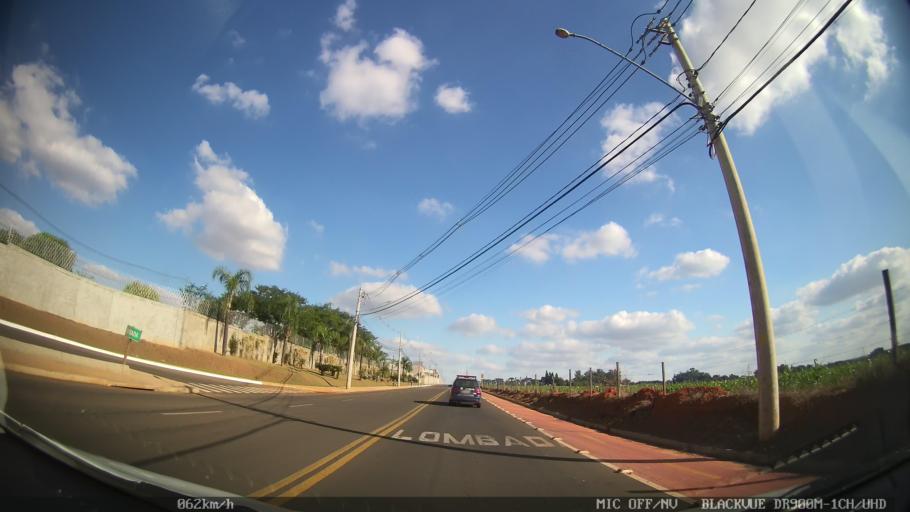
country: BR
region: Sao Paulo
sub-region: Nova Odessa
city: Nova Odessa
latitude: -22.8066
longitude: -47.3193
